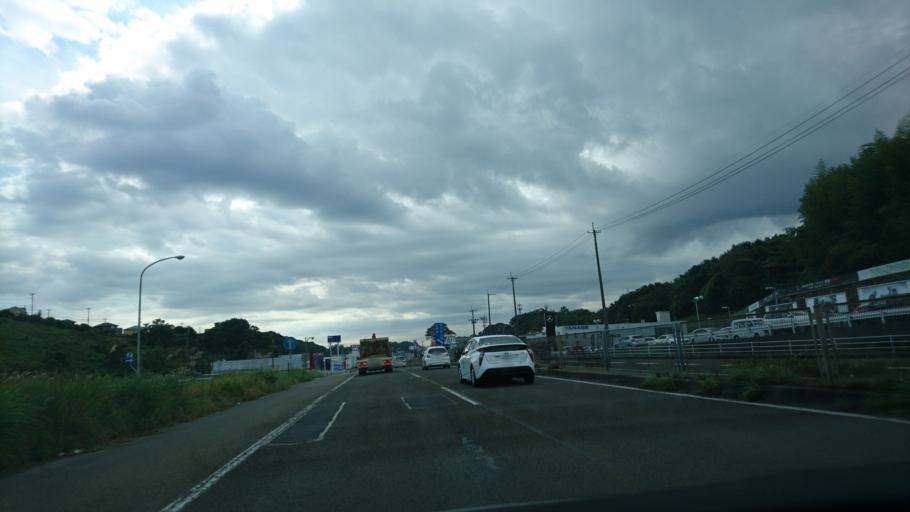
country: JP
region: Miyagi
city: Tomiya
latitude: 38.3433
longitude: 140.8805
